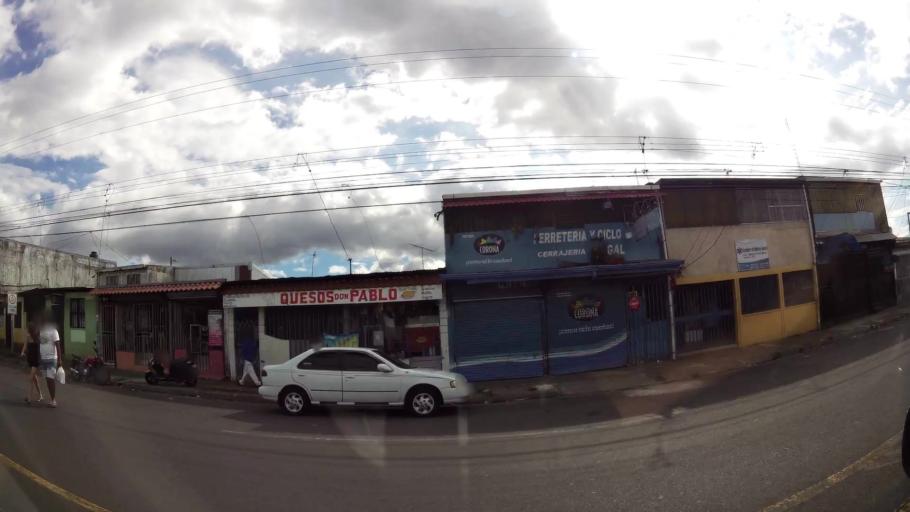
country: CR
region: Heredia
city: La Asuncion
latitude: 9.9585
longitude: -84.1606
